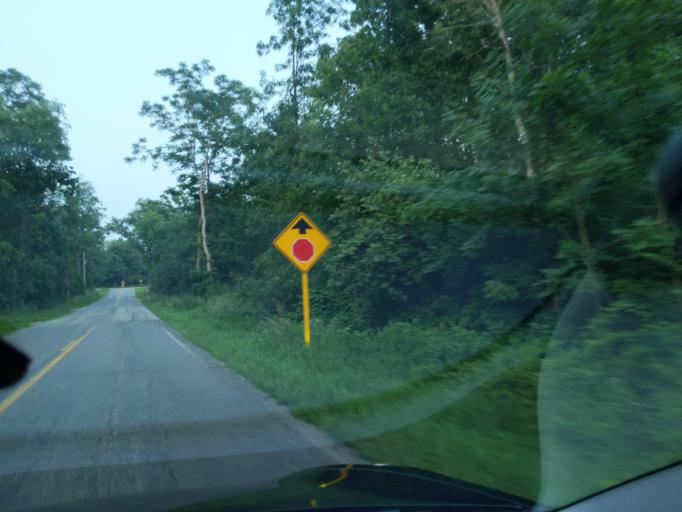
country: US
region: Michigan
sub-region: Jackson County
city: Jackson
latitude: 42.3275
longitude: -84.4164
